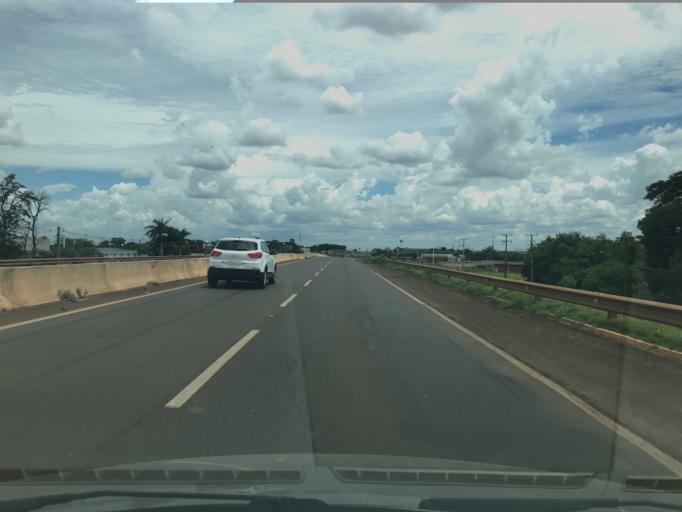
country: BR
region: Parana
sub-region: Paicandu
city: Paicandu
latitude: -23.4495
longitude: -52.0046
